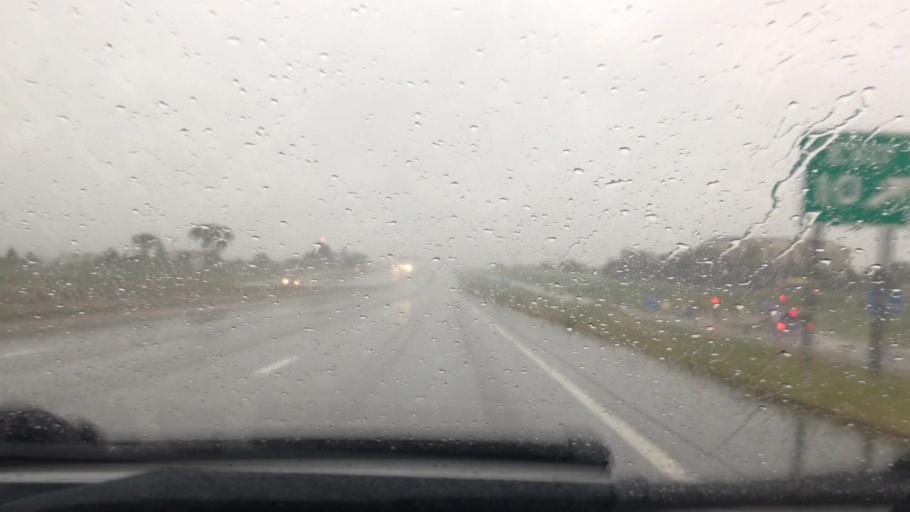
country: US
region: Missouri
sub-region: Platte County
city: Weatherby Lake
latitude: 39.2751
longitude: -94.6709
